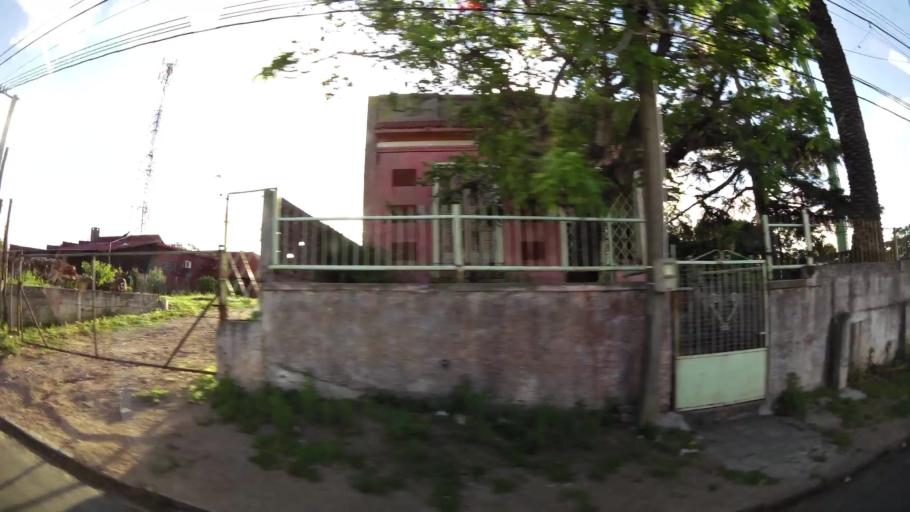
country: UY
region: Montevideo
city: Montevideo
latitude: -34.8776
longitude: -56.2661
